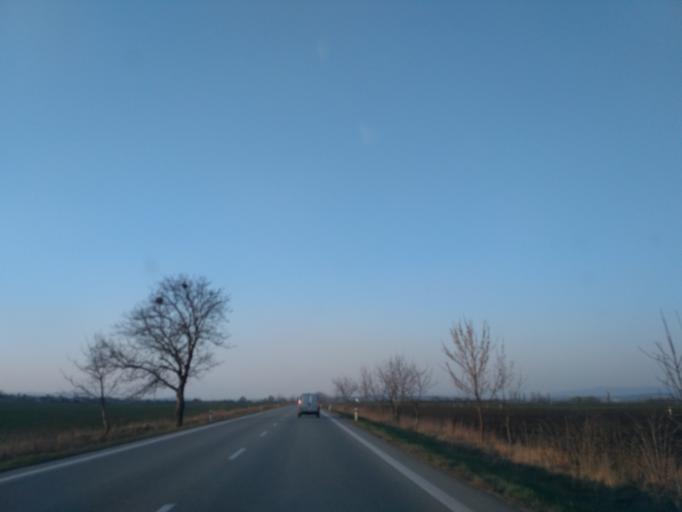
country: SK
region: Kosicky
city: Kosice
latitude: 48.6051
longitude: 21.2626
